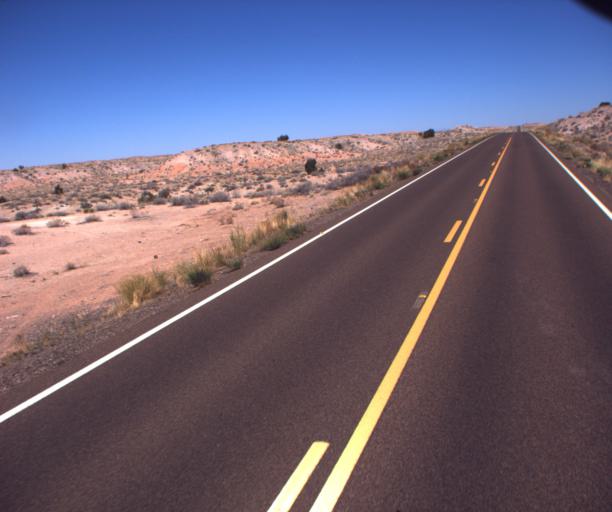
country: US
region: Arizona
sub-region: Navajo County
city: Dilkon
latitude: 35.1901
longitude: -110.4421
